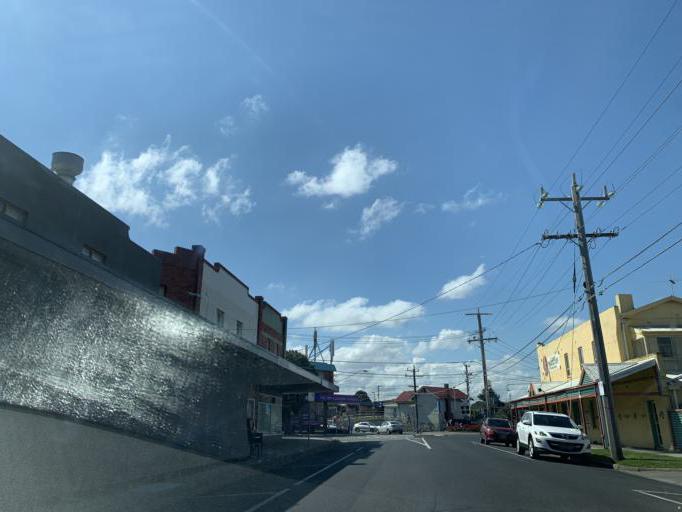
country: AU
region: Victoria
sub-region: Kingston
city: Parkdale
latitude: -37.9944
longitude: 145.0766
